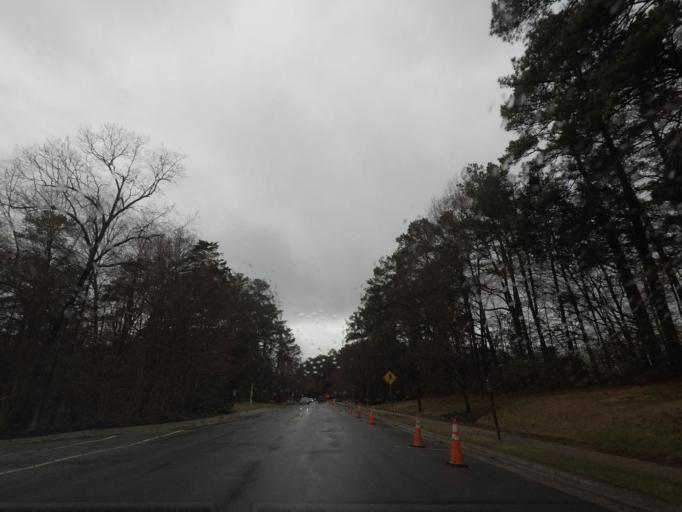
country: US
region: North Carolina
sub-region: Durham County
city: Durham
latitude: 36.0007
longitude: -78.9456
